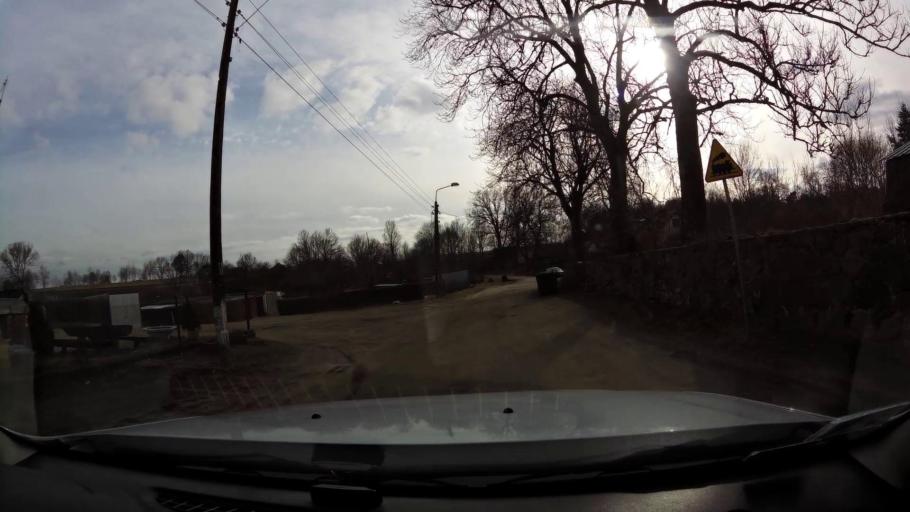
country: PL
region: West Pomeranian Voivodeship
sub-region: Powiat drawski
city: Drawsko Pomorskie
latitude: 53.5158
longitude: 15.7503
